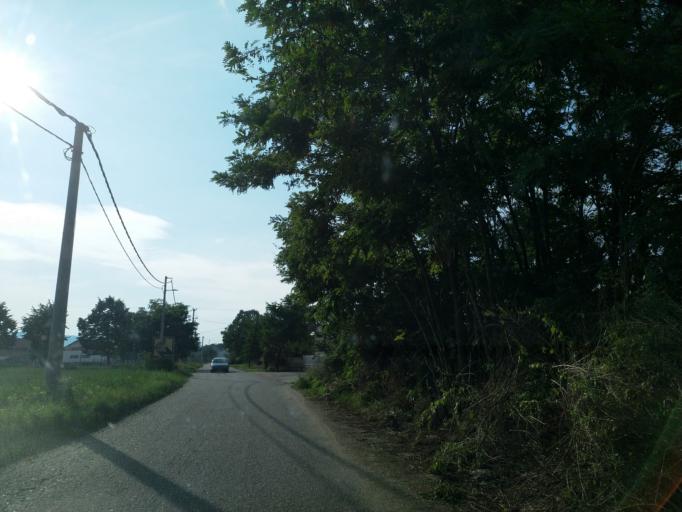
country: RS
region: Central Serbia
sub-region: Pomoravski Okrug
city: Jagodina
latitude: 43.9848
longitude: 21.2186
